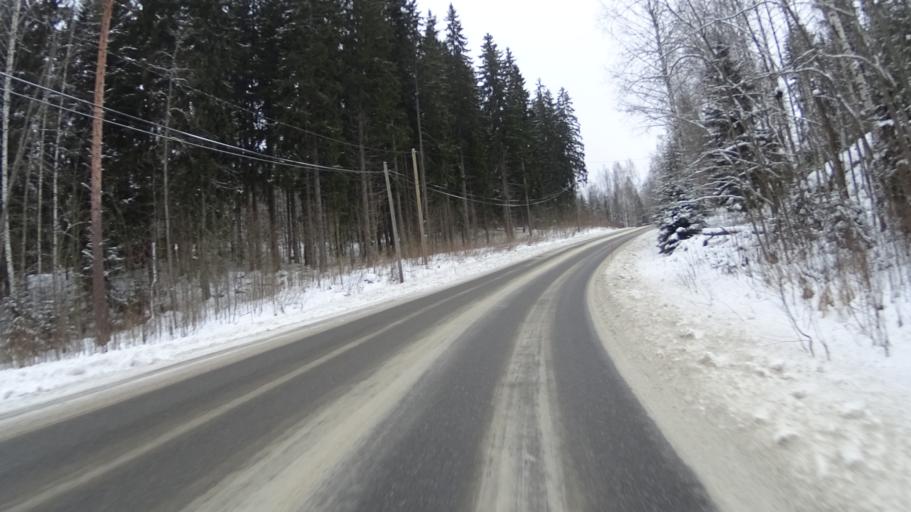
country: FI
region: Uusimaa
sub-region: Helsinki
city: Karkkila
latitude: 60.5078
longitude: 24.1472
